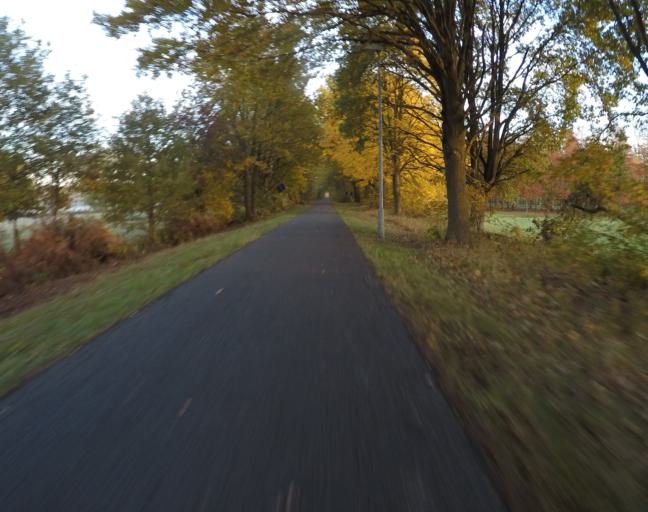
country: BE
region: Flanders
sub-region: Provincie Antwerpen
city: Hulshout
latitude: 51.0537
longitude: 4.8250
